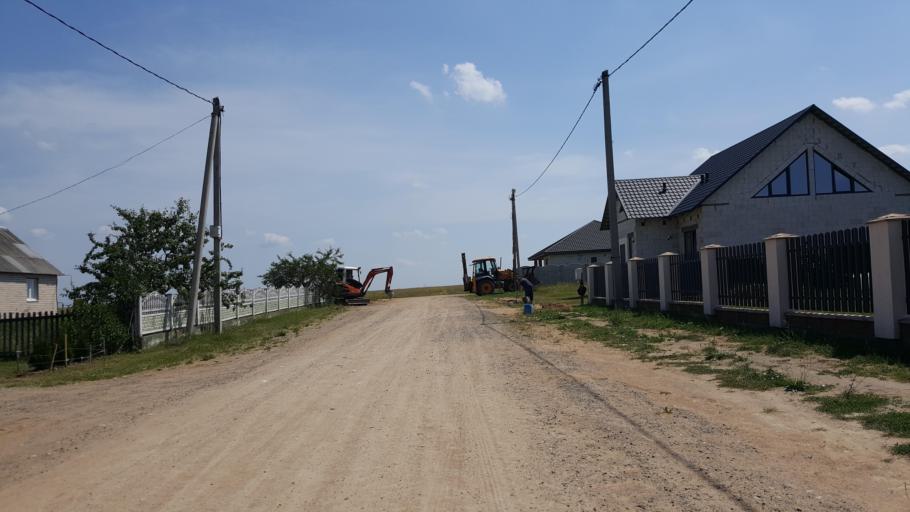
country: BY
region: Brest
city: Kamyanyets
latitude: 52.4050
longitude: 23.8469
